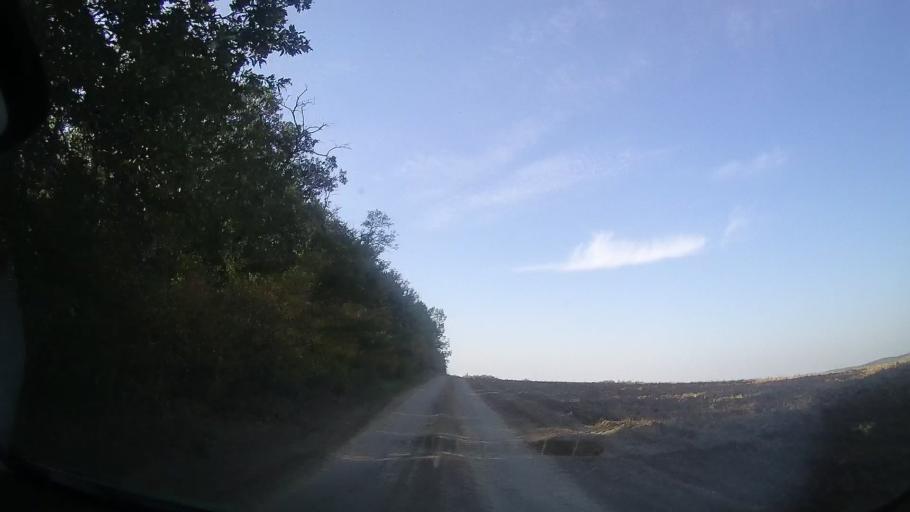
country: RO
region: Timis
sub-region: Comuna Bogda
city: Bogda
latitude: 45.9053
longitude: 21.5784
